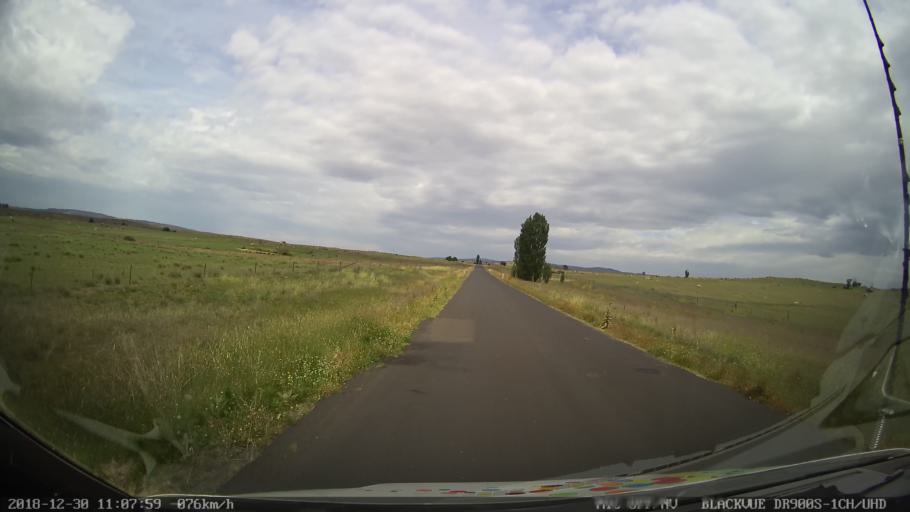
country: AU
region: New South Wales
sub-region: Snowy River
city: Berridale
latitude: -36.5021
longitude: 148.8128
